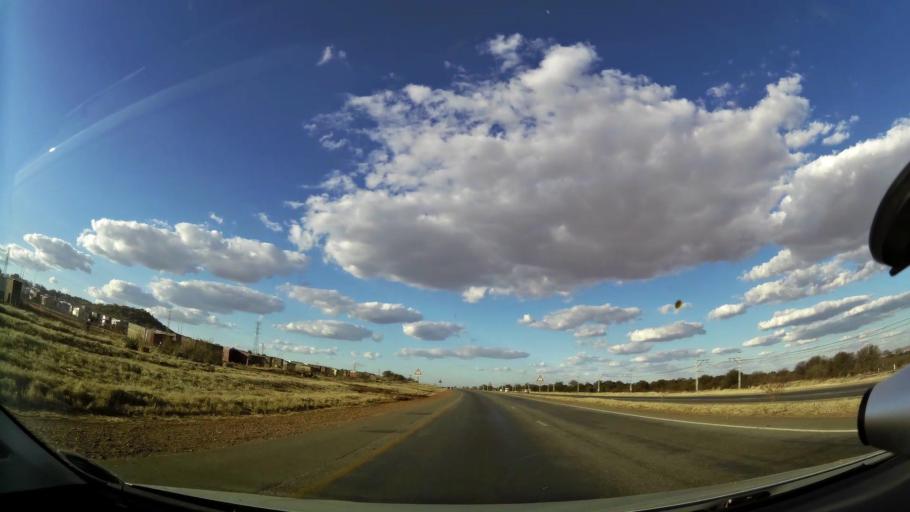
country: ZA
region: North-West
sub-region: Dr Kenneth Kaunda District Municipality
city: Potchefstroom
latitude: -26.7386
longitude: 27.0478
